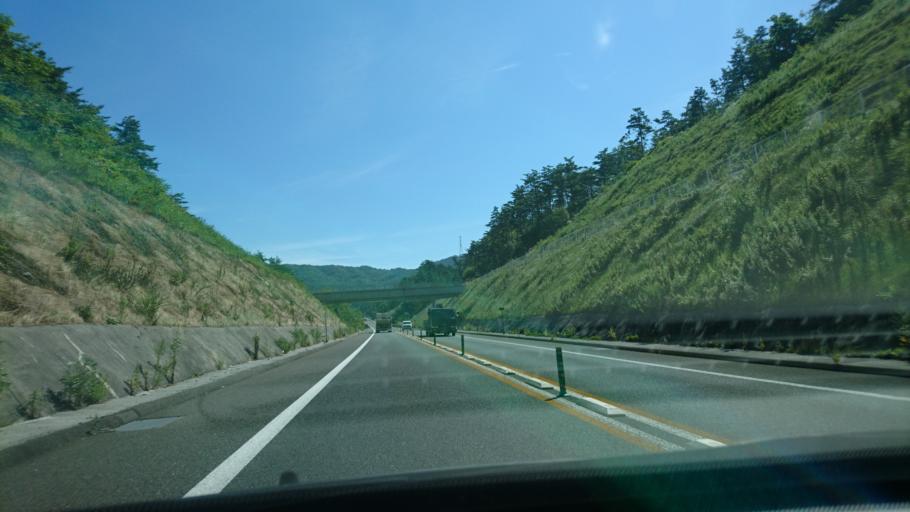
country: JP
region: Iwate
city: Tono
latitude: 39.2894
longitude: 141.3318
